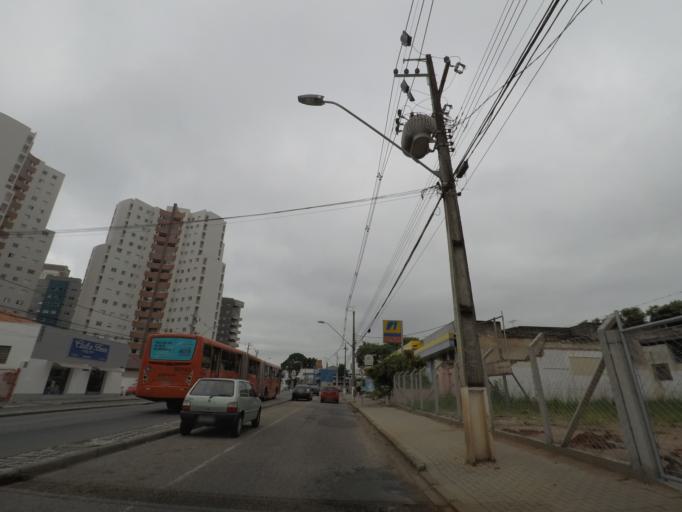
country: BR
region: Parana
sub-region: Curitiba
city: Curitiba
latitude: -25.4693
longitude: -49.2942
